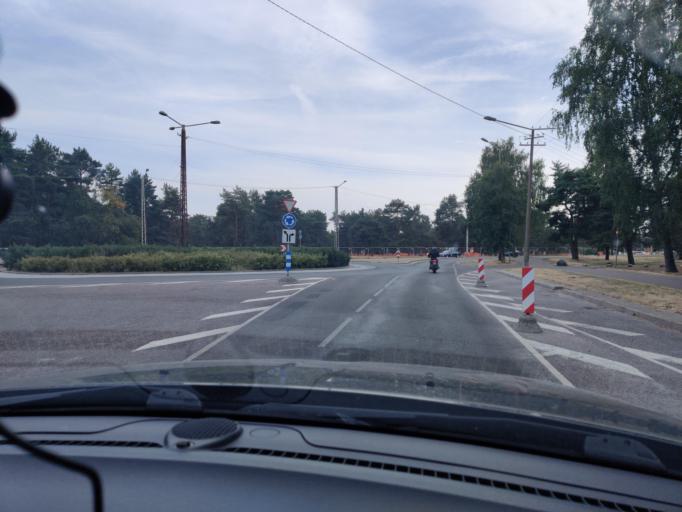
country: EE
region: Harju
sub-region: Saue vald
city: Laagri
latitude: 59.4017
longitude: 24.6779
